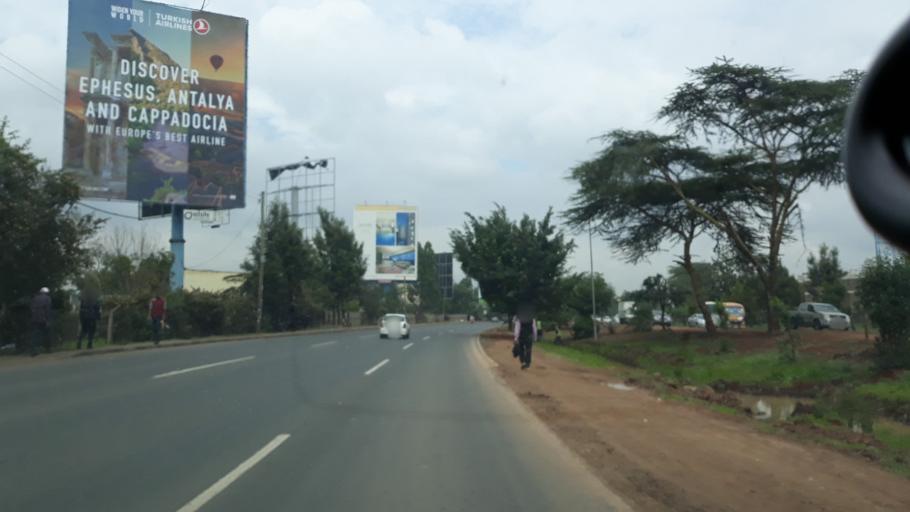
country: KE
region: Nairobi Area
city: Nairobi
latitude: -1.3159
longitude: 36.8322
